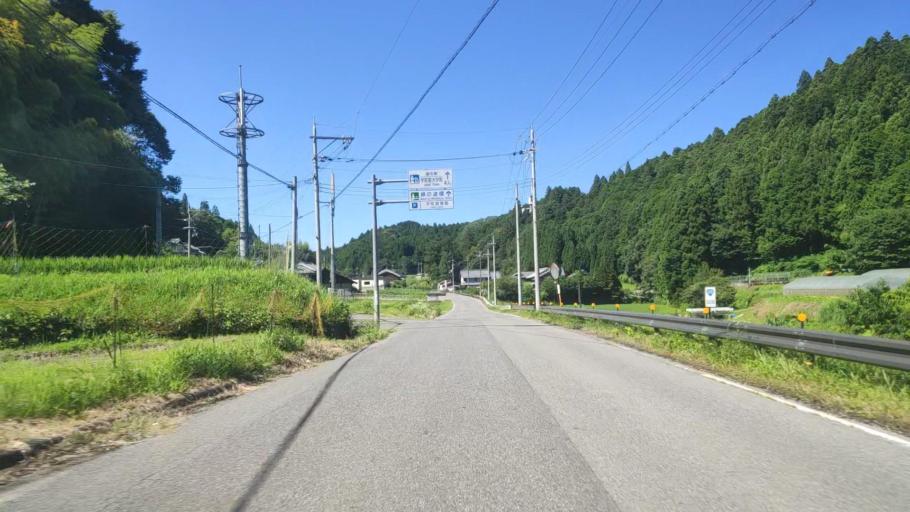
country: JP
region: Nara
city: Yoshino-cho
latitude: 34.4412
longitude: 135.9376
